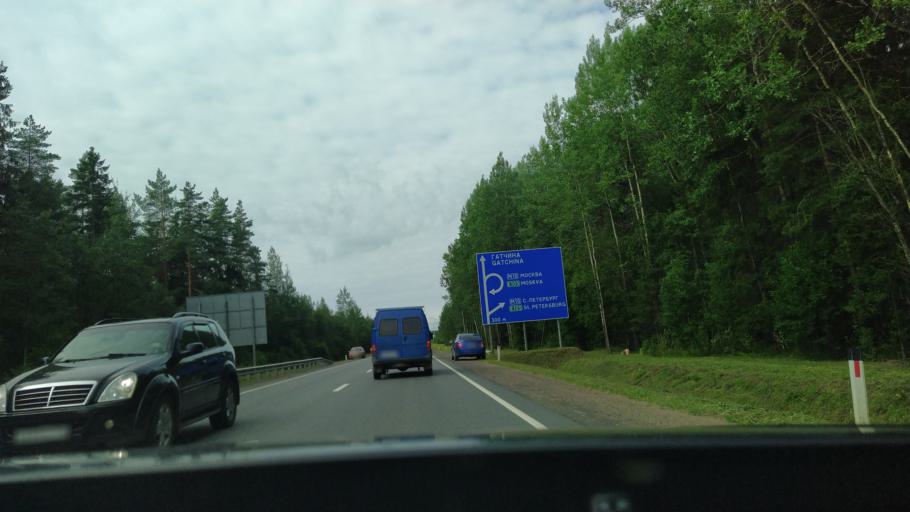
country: RU
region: Leningrad
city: Ul'yanovka
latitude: 59.6104
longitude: 30.7693
